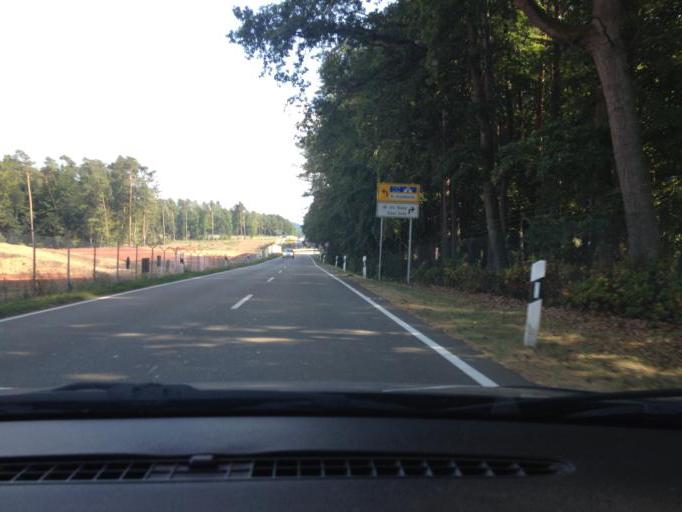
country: DE
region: Rheinland-Pfalz
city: Mackenbach
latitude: 49.4524
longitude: 7.6095
